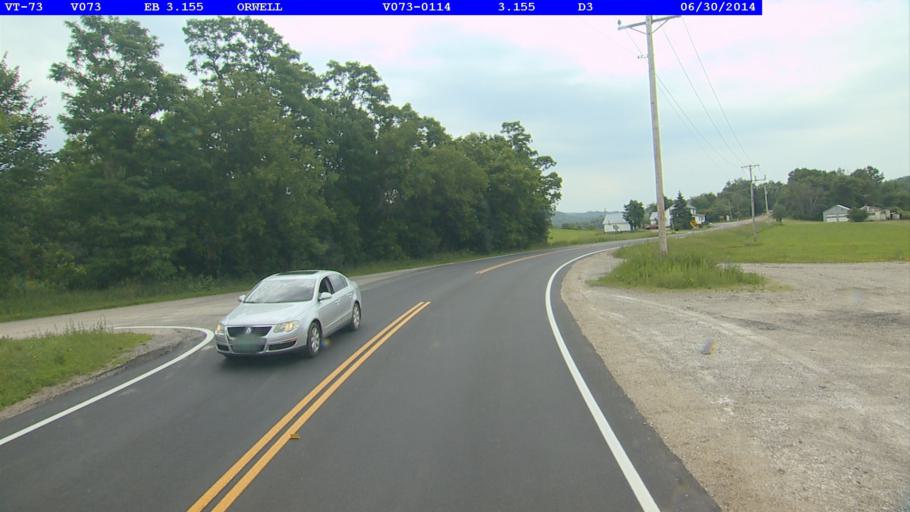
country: US
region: Vermont
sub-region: Rutland County
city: Brandon
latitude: 43.8013
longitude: -73.2444
